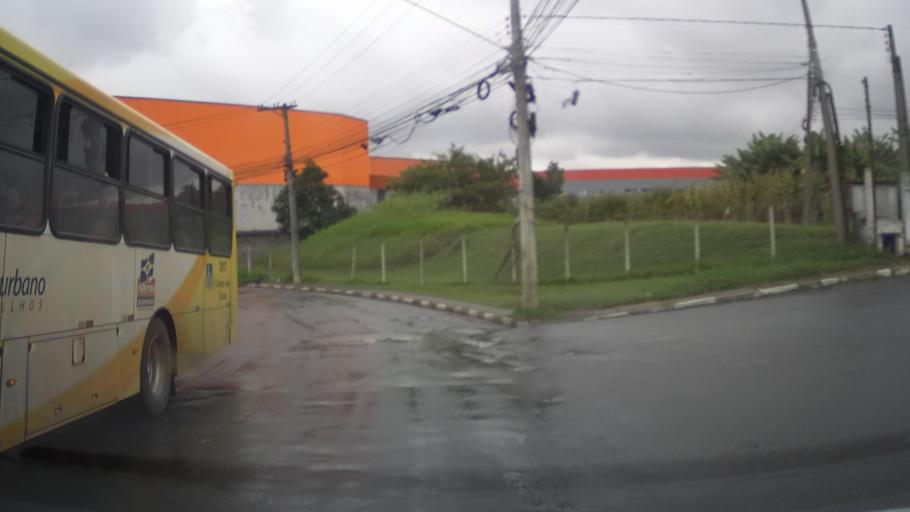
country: BR
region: Sao Paulo
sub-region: Guarulhos
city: Guarulhos
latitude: -23.4751
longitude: -46.4441
